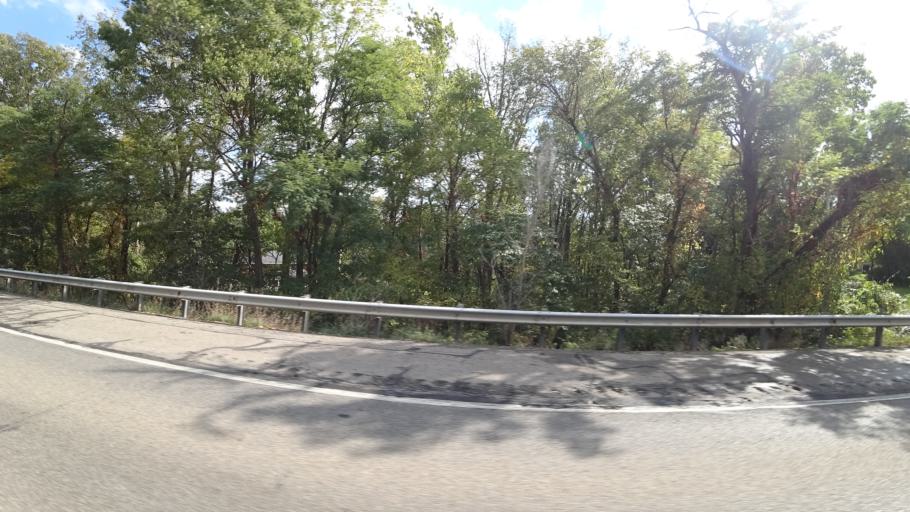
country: US
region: Michigan
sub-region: Branch County
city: Union City
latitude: 42.0858
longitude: -85.1200
